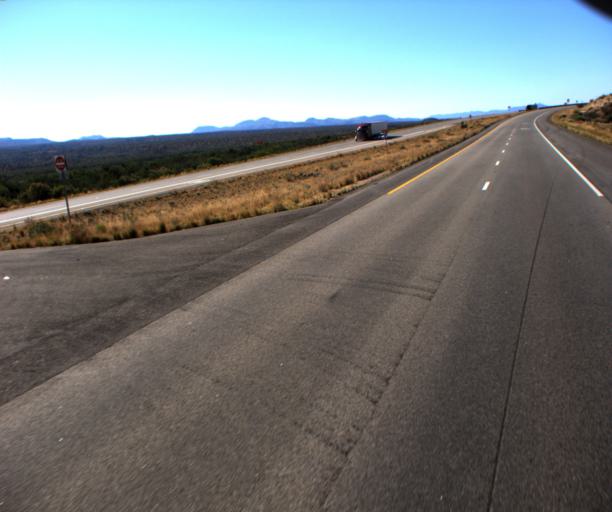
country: US
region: Arizona
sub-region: Yavapai County
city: Bagdad
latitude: 34.8236
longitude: -113.6277
